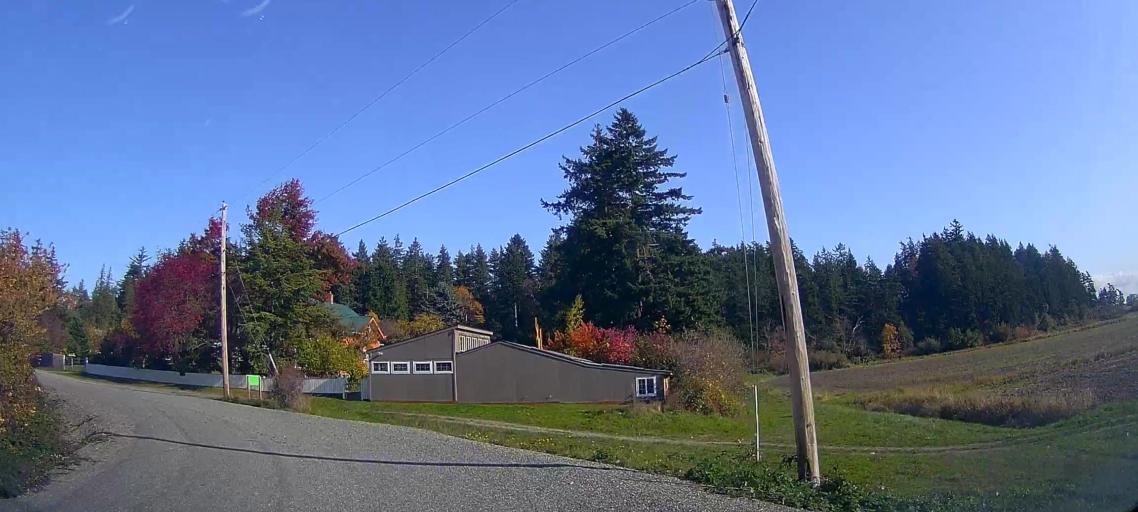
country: US
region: Washington
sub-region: Skagit County
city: Mount Vernon
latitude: 48.3634
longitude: -122.4426
